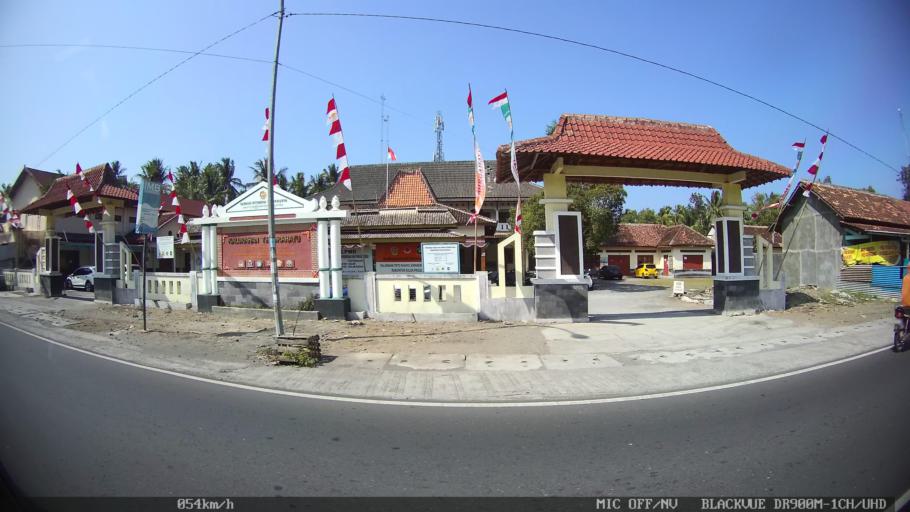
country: ID
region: Daerah Istimewa Yogyakarta
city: Srandakan
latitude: -7.9298
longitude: 110.2017
